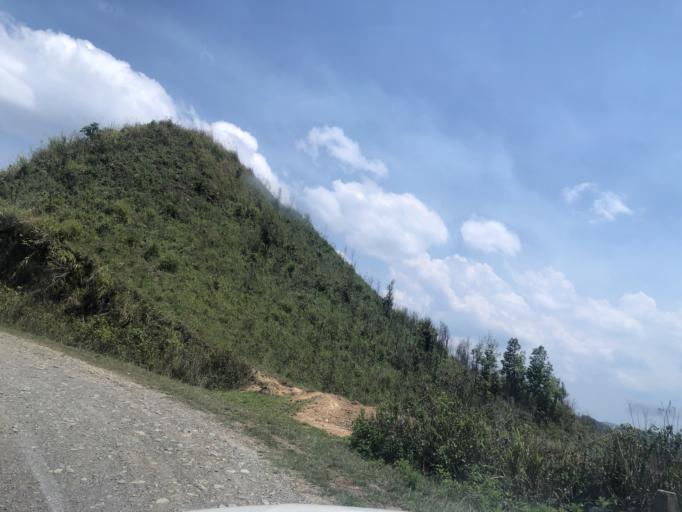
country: LA
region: Phongsali
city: Phongsali
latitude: 21.4152
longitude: 102.1849
